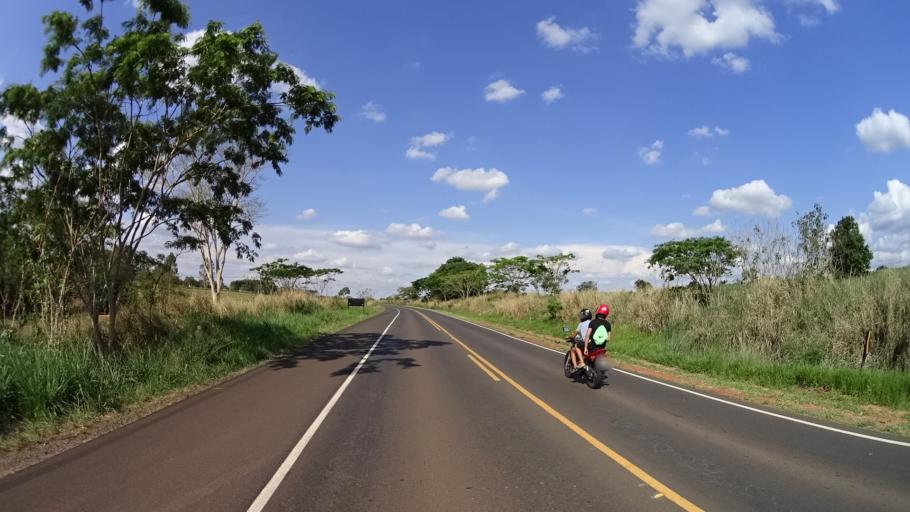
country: BR
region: Sao Paulo
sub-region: Urupes
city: Urupes
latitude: -21.0069
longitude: -49.2187
